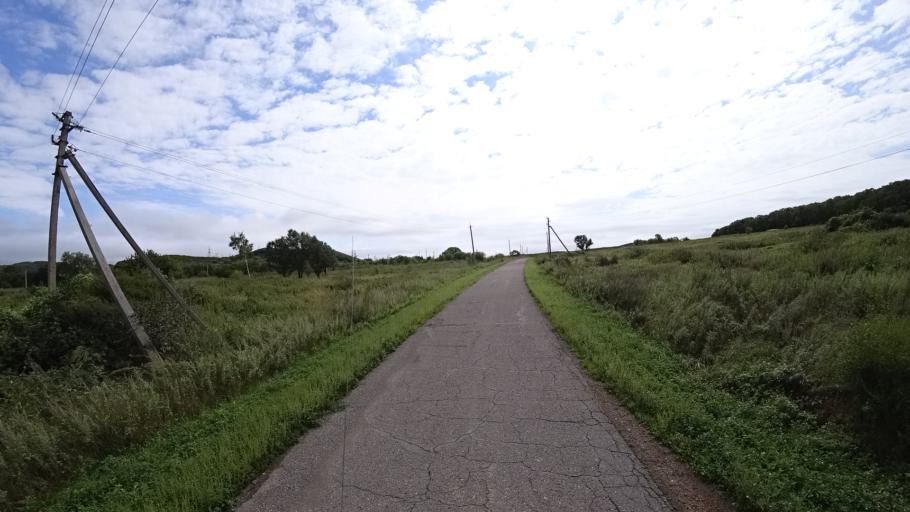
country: RU
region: Primorskiy
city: Lyalichi
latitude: 44.1348
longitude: 132.3879
